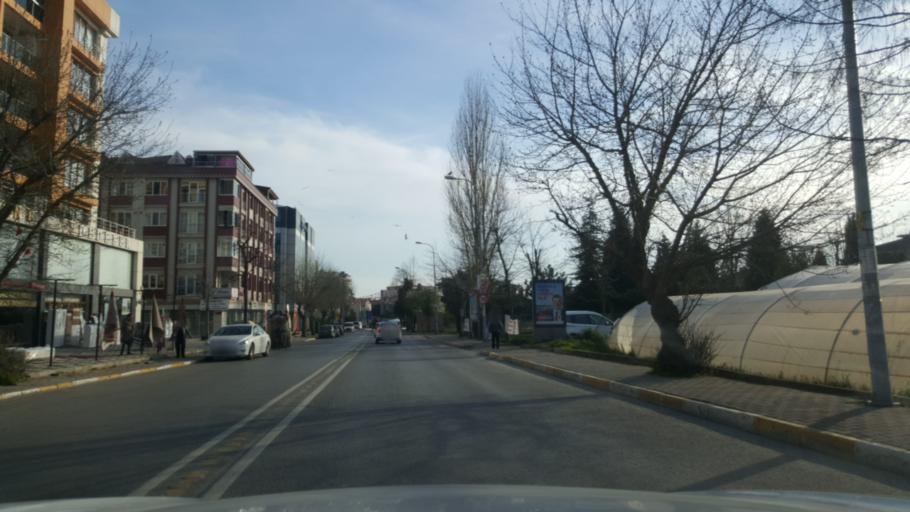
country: TR
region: Istanbul
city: Icmeler
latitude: 40.8233
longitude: 29.3099
